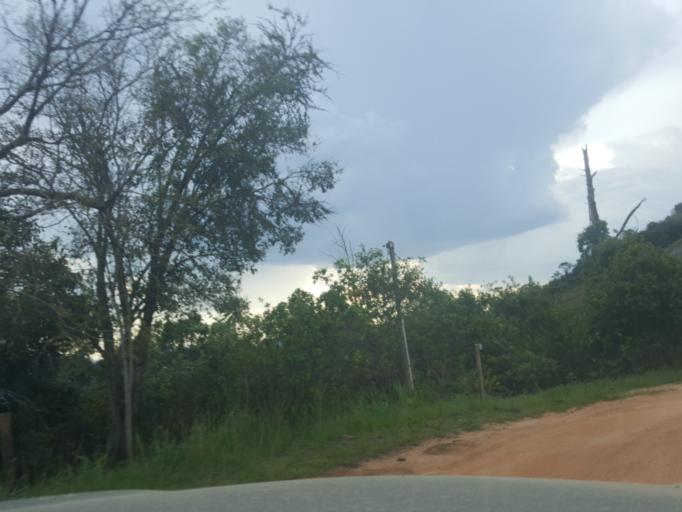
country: ZA
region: Limpopo
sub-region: Mopani District Municipality
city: Hoedspruit
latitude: -24.5811
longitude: 30.8639
